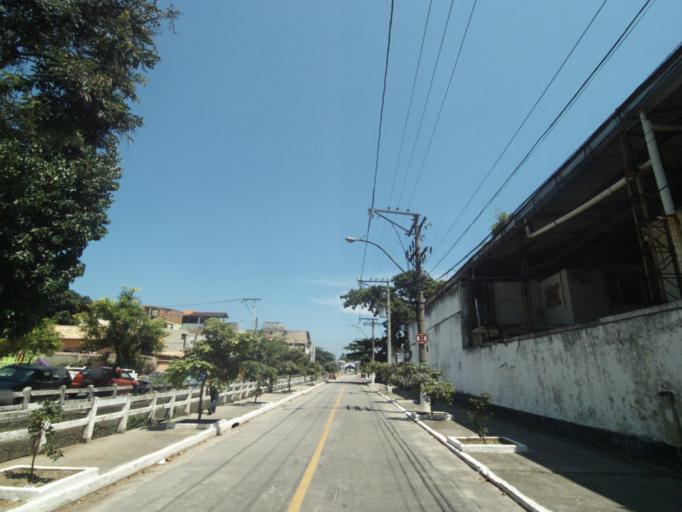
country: BR
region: Rio de Janeiro
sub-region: Niteroi
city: Niteroi
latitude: -22.9347
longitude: -43.1134
